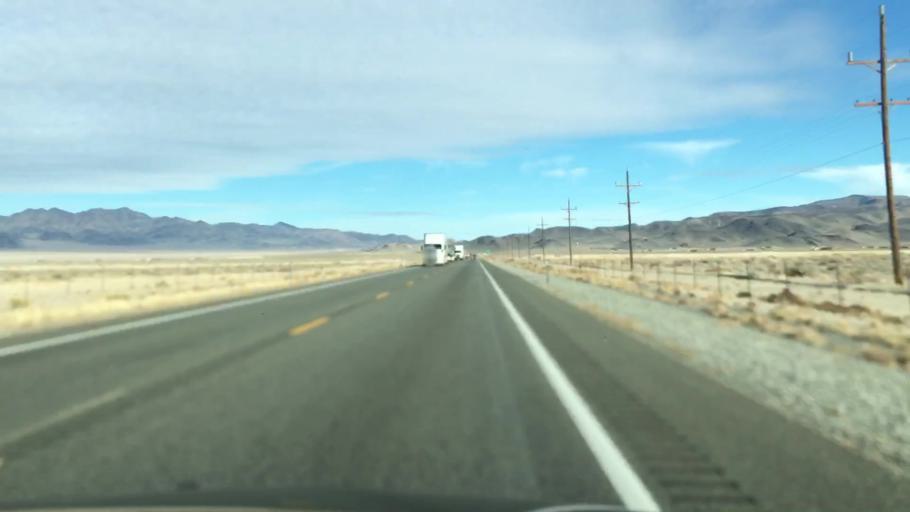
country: US
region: Nevada
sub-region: Mineral County
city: Hawthorne
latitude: 38.5268
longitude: -118.5662
